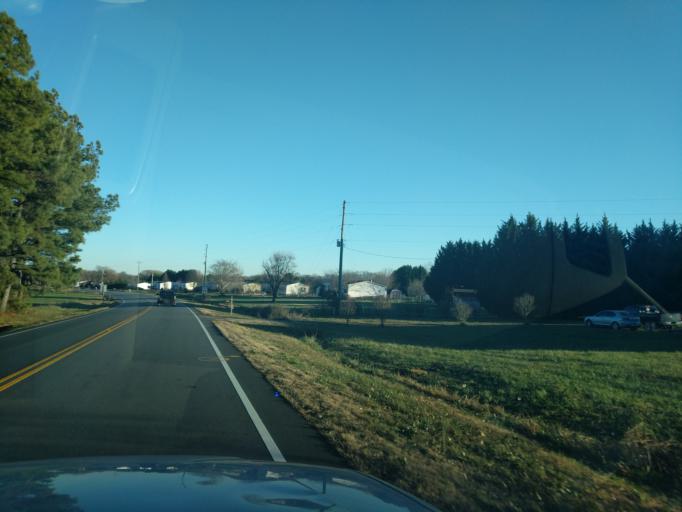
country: US
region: South Carolina
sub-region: Oconee County
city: Utica
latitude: 34.5945
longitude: -82.9721
